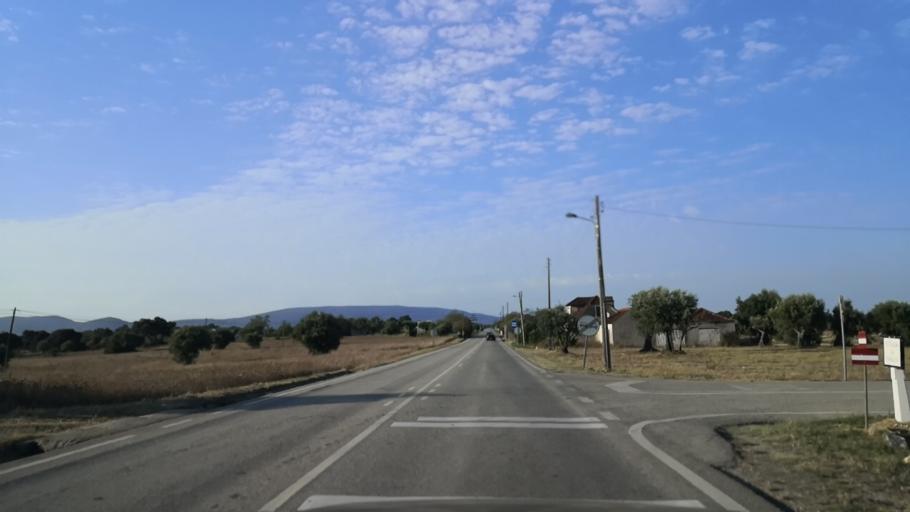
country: PT
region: Santarem
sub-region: Alcanena
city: Alcanena
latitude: 39.4089
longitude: -8.6387
